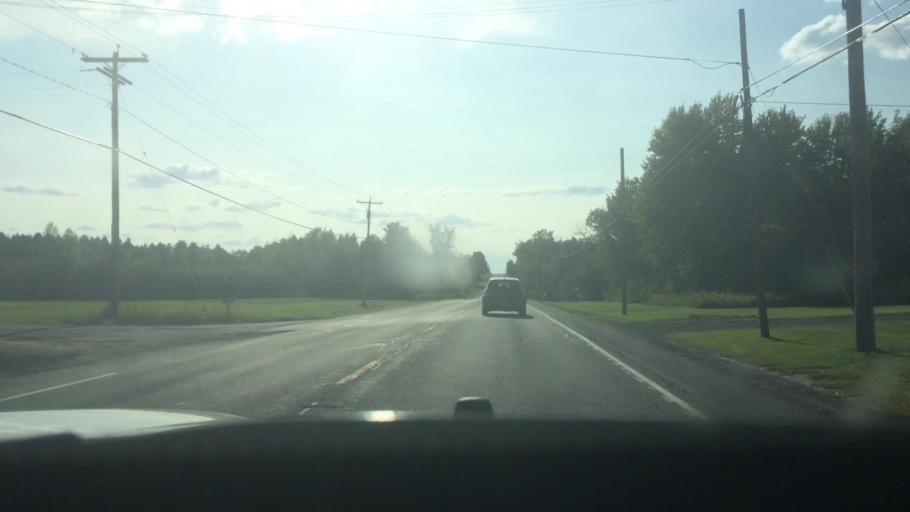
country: US
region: New York
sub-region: St. Lawrence County
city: Potsdam
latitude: 44.6702
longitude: -74.9270
